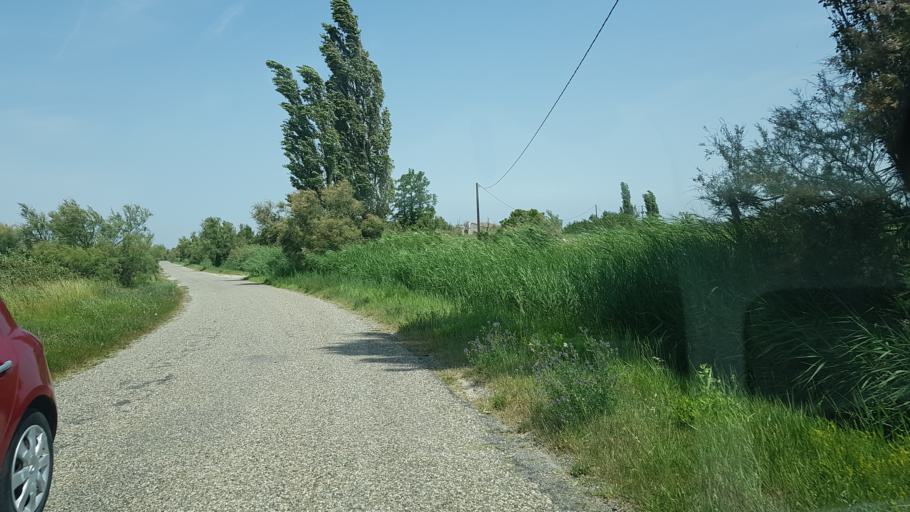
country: FR
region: Provence-Alpes-Cote d'Azur
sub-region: Departement des Bouches-du-Rhone
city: Arles
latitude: 43.5298
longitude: 4.6411
